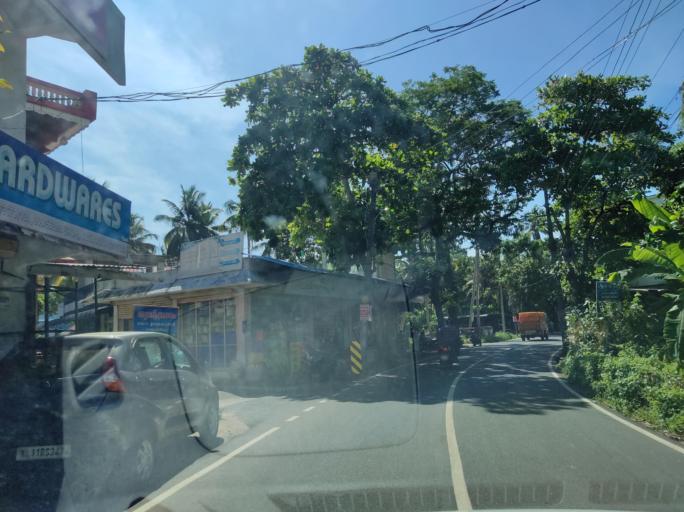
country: IN
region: Kerala
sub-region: Alappuzha
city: Kayankulam
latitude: 9.2598
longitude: 76.4096
